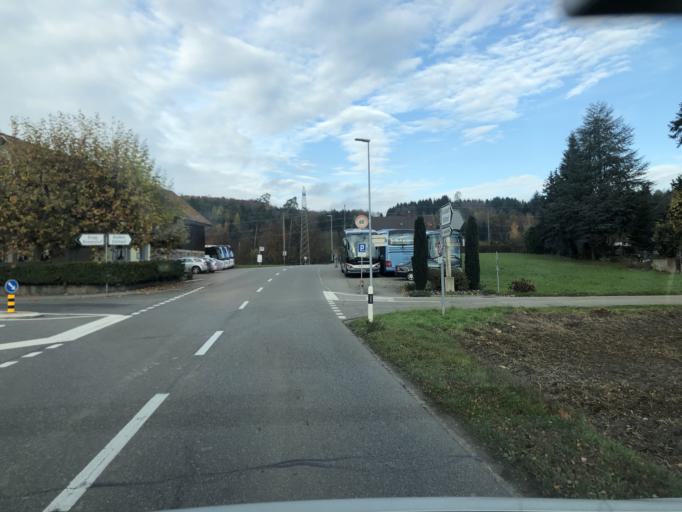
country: CH
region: Aargau
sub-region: Bezirk Baden
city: Mellingen
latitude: 47.4432
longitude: 8.2812
